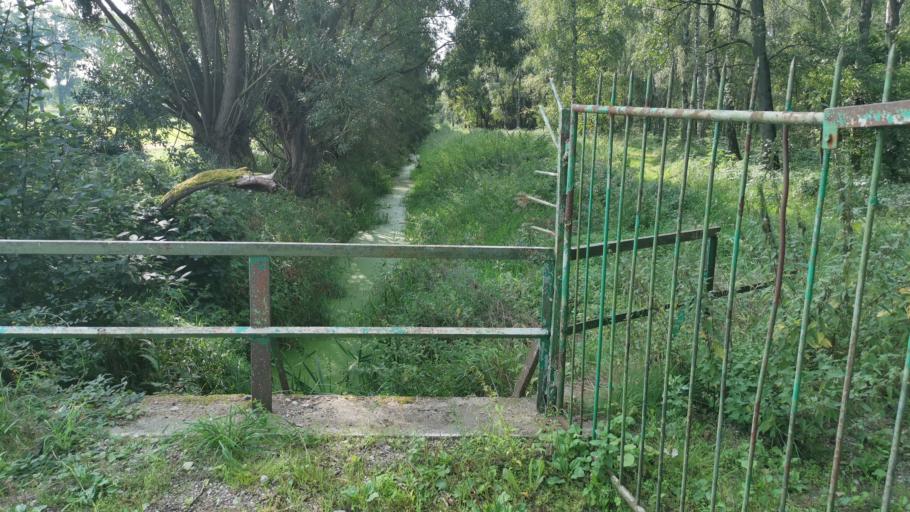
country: DE
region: Schleswig-Holstein
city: Lehmrade
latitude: 53.5939
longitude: 10.7800
